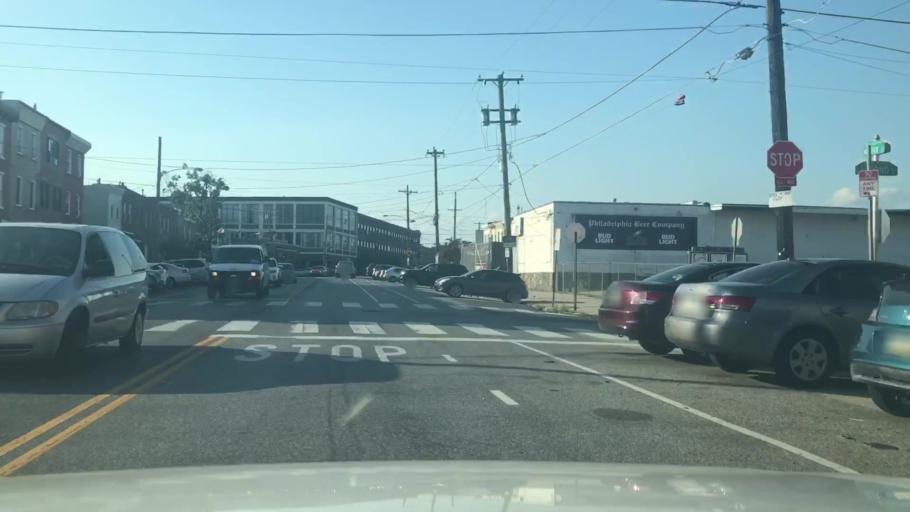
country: US
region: Pennsylvania
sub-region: Philadelphia County
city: Philadelphia
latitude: 39.9763
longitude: -75.1226
